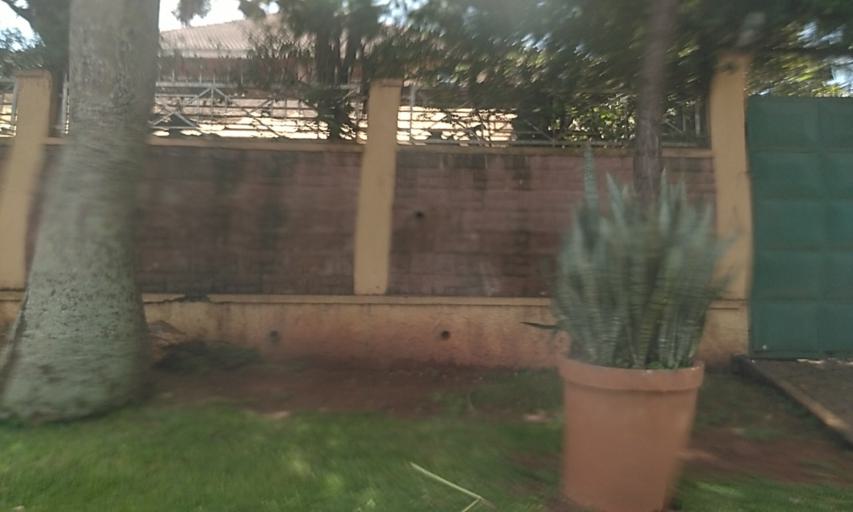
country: UG
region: Central Region
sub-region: Kampala District
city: Kampala
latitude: 0.3323
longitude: 32.6011
